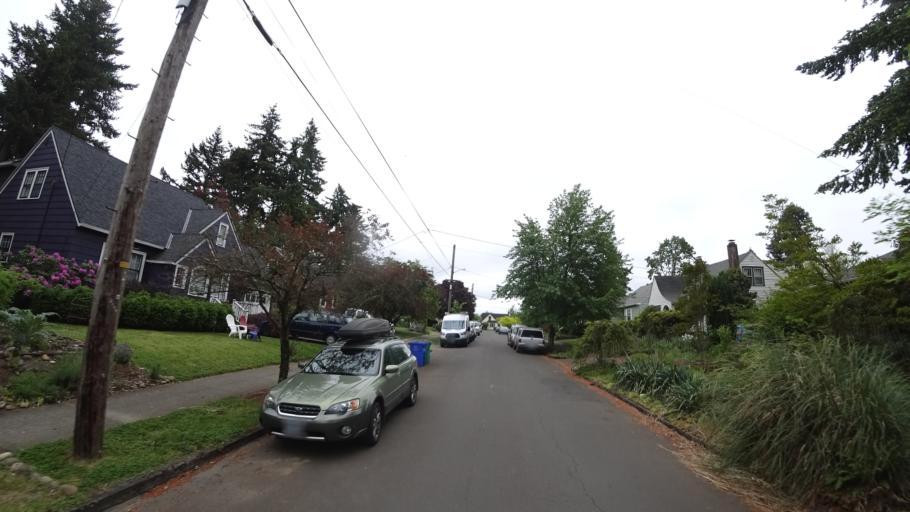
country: US
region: Oregon
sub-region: Multnomah County
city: Portland
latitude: 45.5515
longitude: -122.6224
